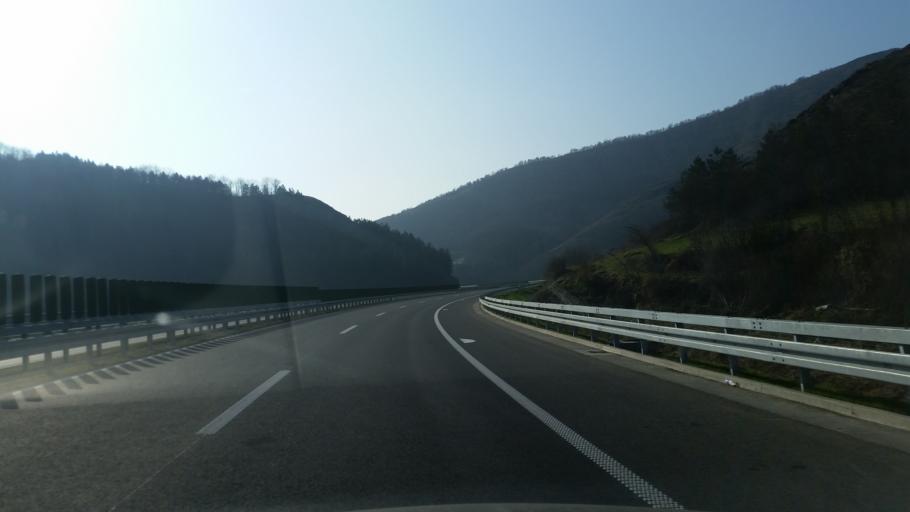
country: RS
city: Prislonica
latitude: 43.9957
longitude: 20.4030
